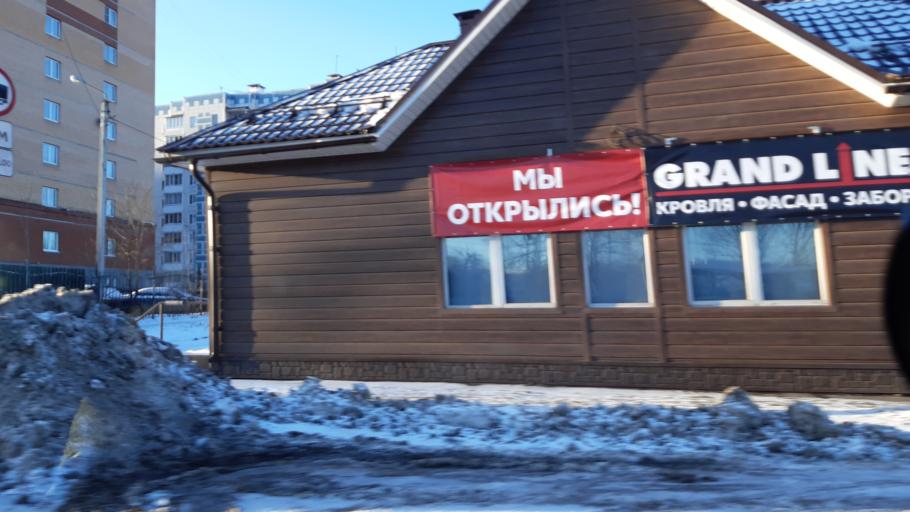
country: RU
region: Moskovskaya
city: Skoropuskovskiy
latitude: 56.3345
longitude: 38.1584
